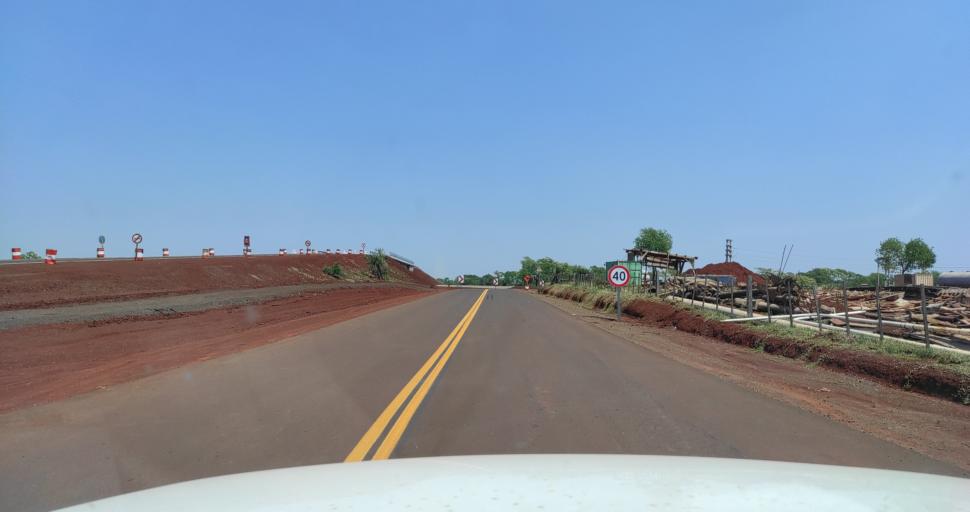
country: AR
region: Misiones
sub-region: Departamento de Candelaria
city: Loreto
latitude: -27.3383
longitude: -55.5428
